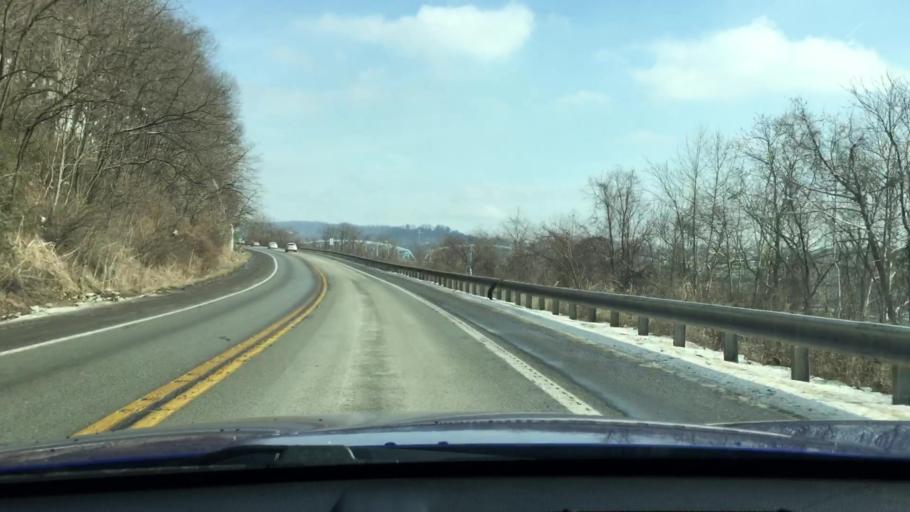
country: US
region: Pennsylvania
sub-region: Allegheny County
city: West Mifflin
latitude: 40.3579
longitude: -79.8531
